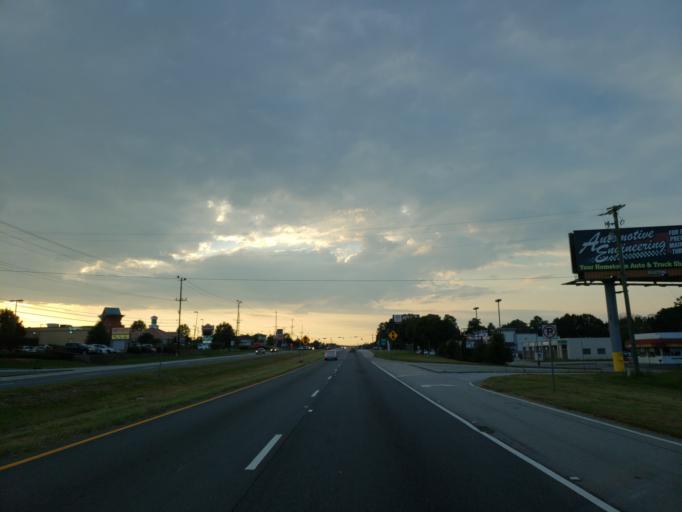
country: US
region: Georgia
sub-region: Paulding County
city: Hiram
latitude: 33.8860
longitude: -84.7373
